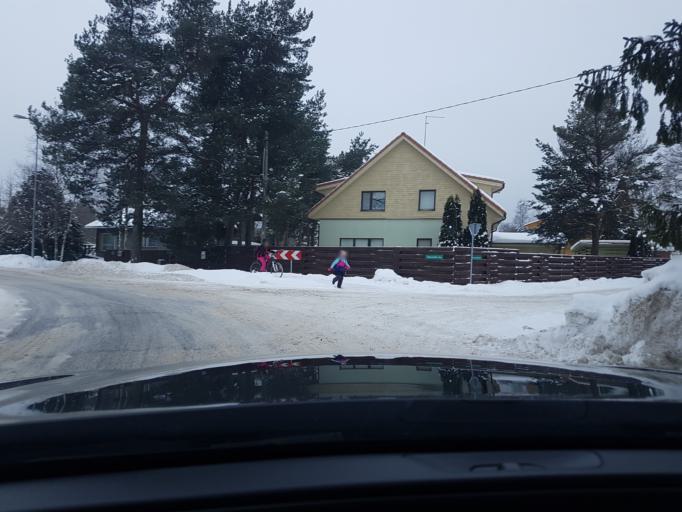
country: EE
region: Harju
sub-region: Saue vald
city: Laagri
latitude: 59.3522
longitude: 24.6357
